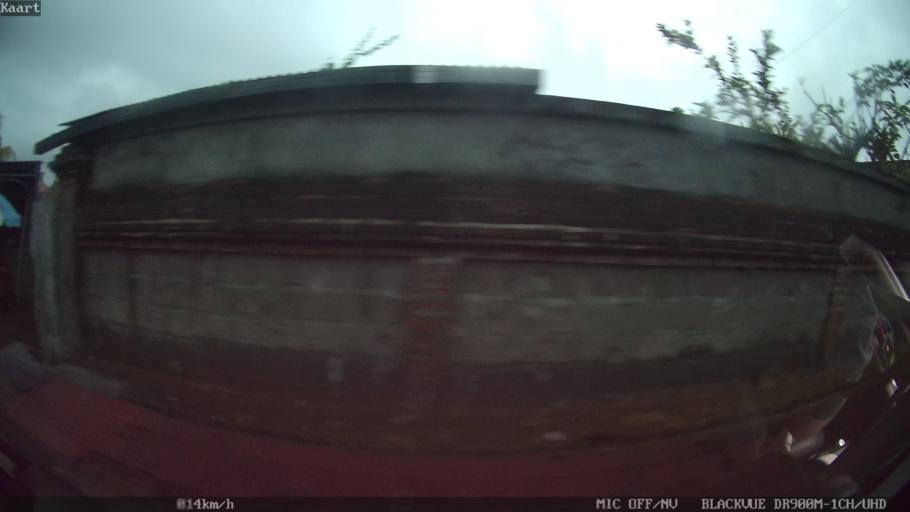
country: ID
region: Bali
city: Banjar Desa
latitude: -8.5752
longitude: 115.2591
